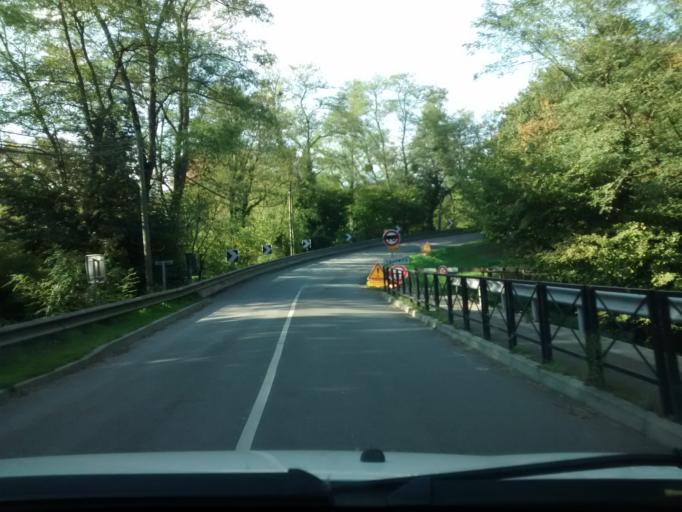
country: FR
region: Pays de la Loire
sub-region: Departement de la Loire-Atlantique
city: Sautron
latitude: 47.2685
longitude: -1.6712
